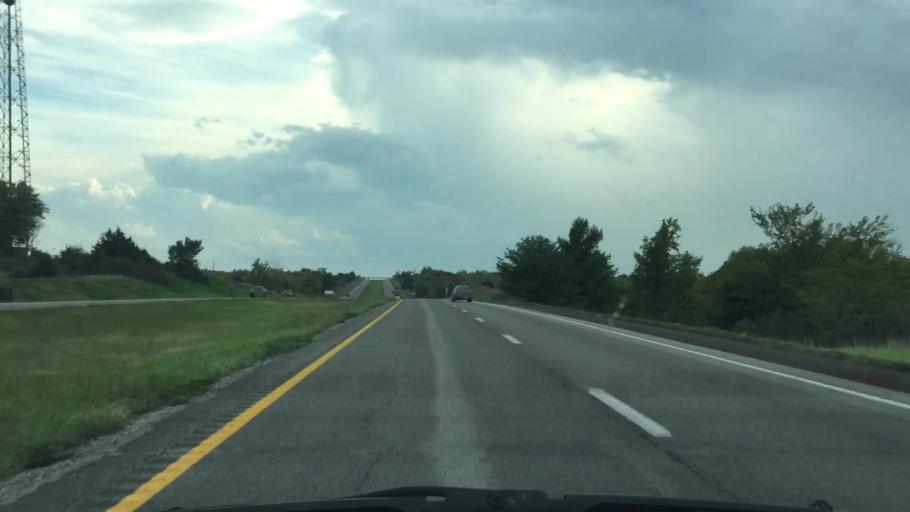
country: US
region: Missouri
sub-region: Clinton County
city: Cameron
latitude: 39.8713
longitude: -94.1675
